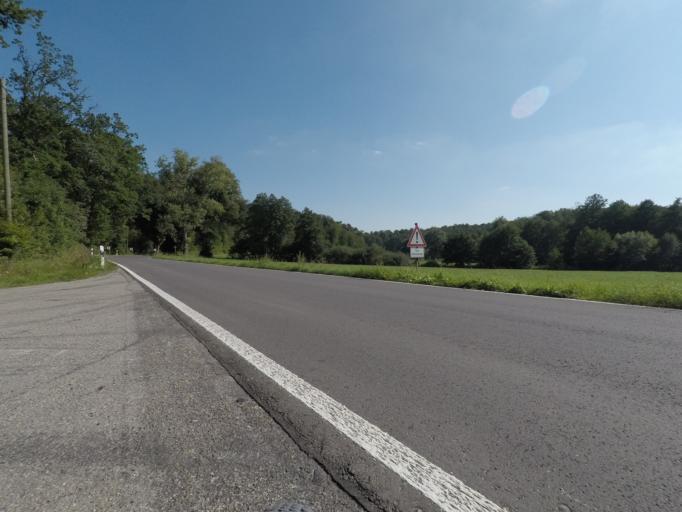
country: DE
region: Baden-Wuerttemberg
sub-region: Regierungsbezirk Stuttgart
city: Ehningen
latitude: 48.6569
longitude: 8.9671
